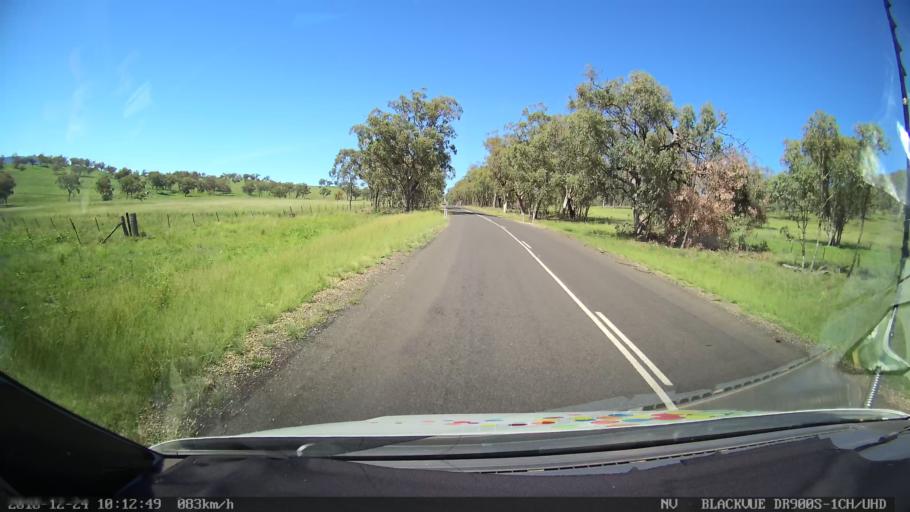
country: AU
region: New South Wales
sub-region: Liverpool Plains
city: Quirindi
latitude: -31.6830
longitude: 150.6444
